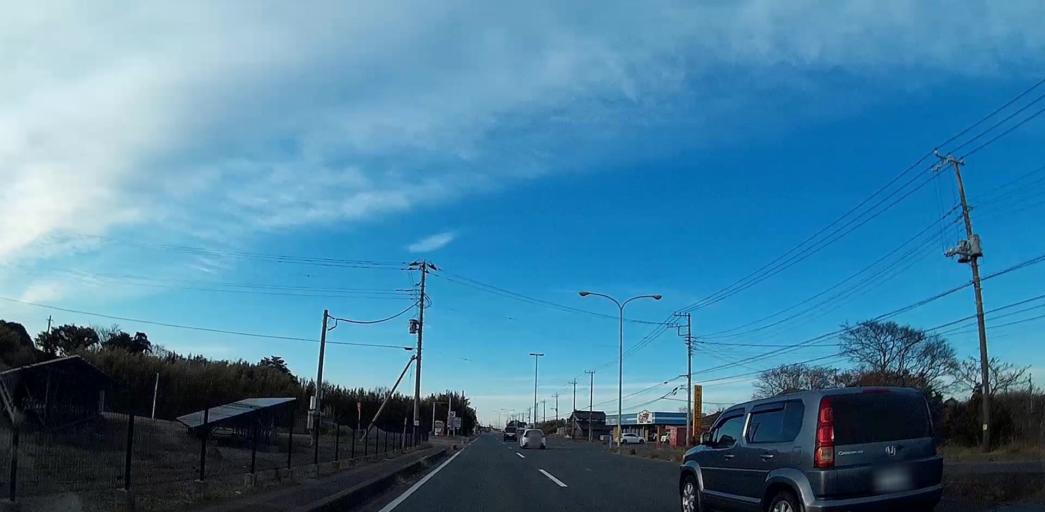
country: JP
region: Chiba
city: Hasaki
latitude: 35.7937
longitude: 140.7577
